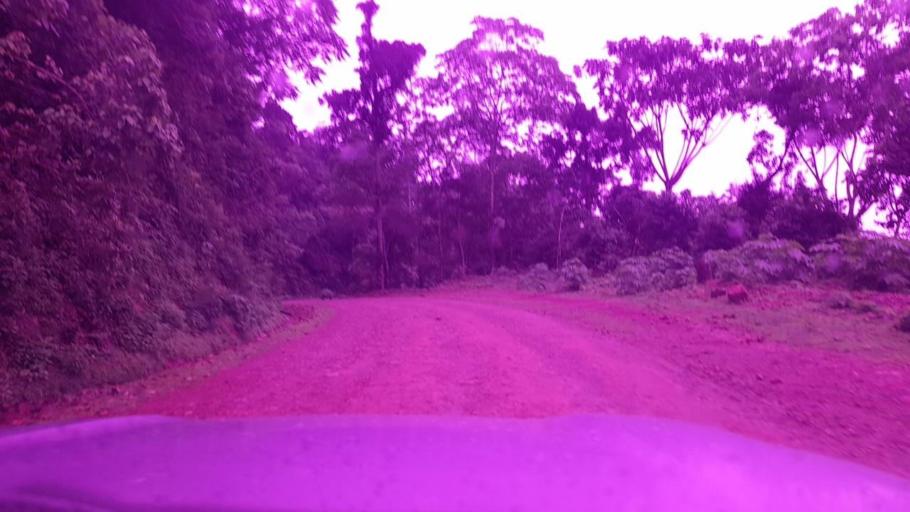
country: ET
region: Southern Nations, Nationalities, and People's Region
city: Bonga
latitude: 7.5104
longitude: 36.0609
